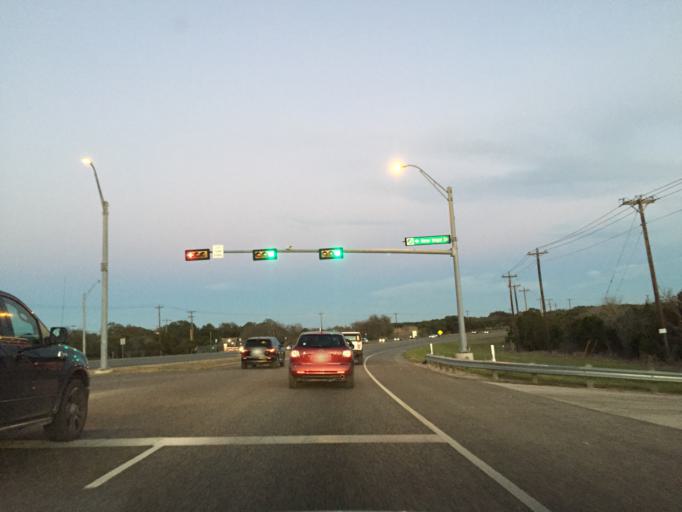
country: US
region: Texas
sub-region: Williamson County
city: Cedar Park
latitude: 30.5155
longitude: -97.8704
